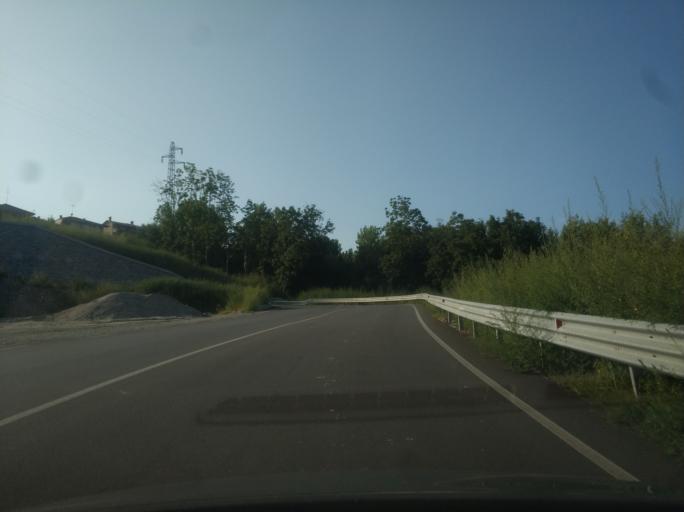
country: IT
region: Piedmont
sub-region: Provincia di Cuneo
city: Roreto
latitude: 44.6712
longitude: 7.8457
